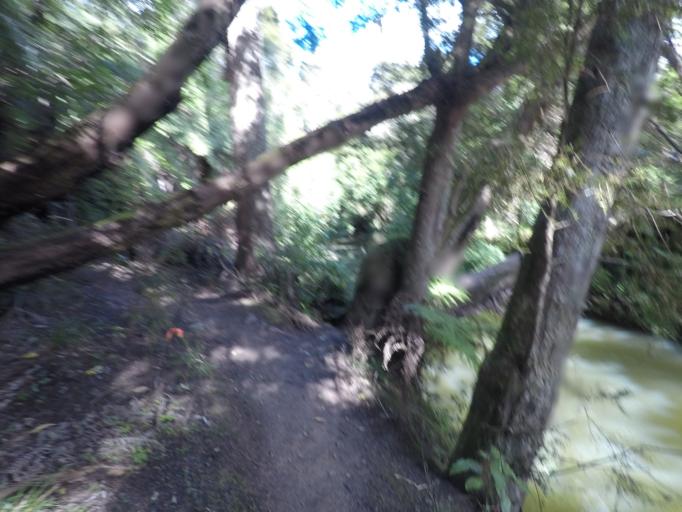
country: NZ
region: Auckland
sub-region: Auckland
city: Rothesay Bay
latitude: -36.7337
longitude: 174.6956
